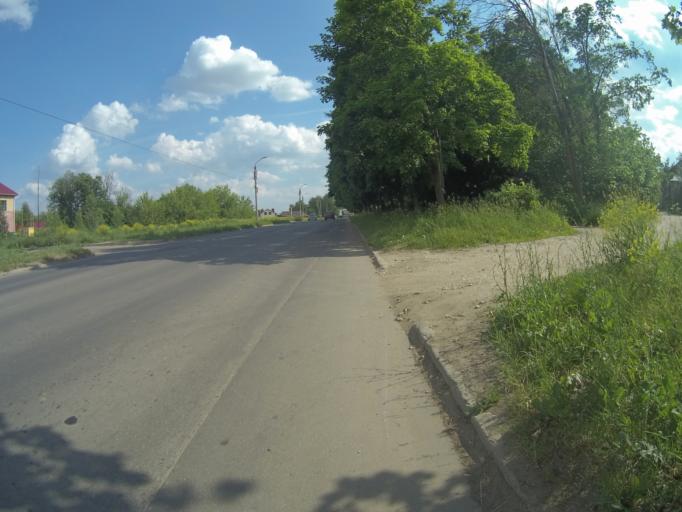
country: RU
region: Vladimir
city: Suzdal'
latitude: 56.4286
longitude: 40.4543
